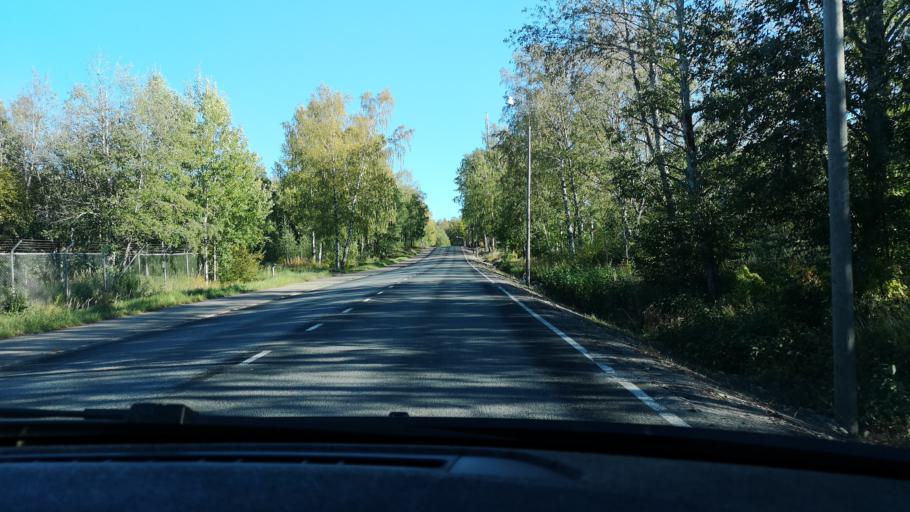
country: FI
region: Ostrobothnia
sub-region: Vaasa
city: Vaasa
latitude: 63.0892
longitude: 21.5710
